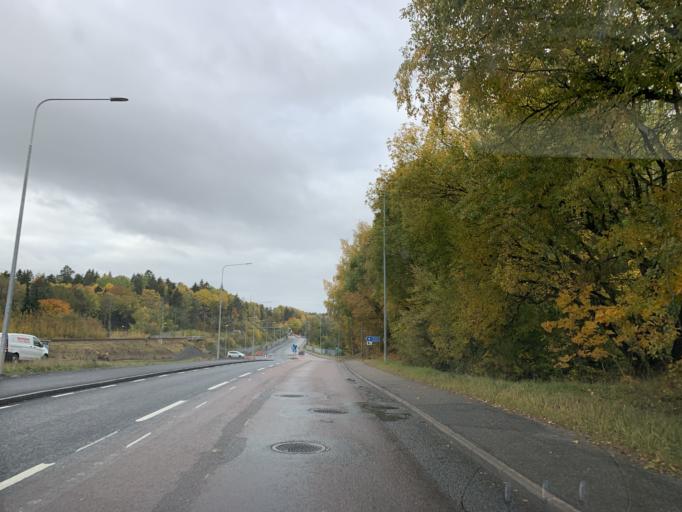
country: SE
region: Stockholm
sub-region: Botkyrka Kommun
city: Tullinge
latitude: 59.2047
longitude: 17.9000
